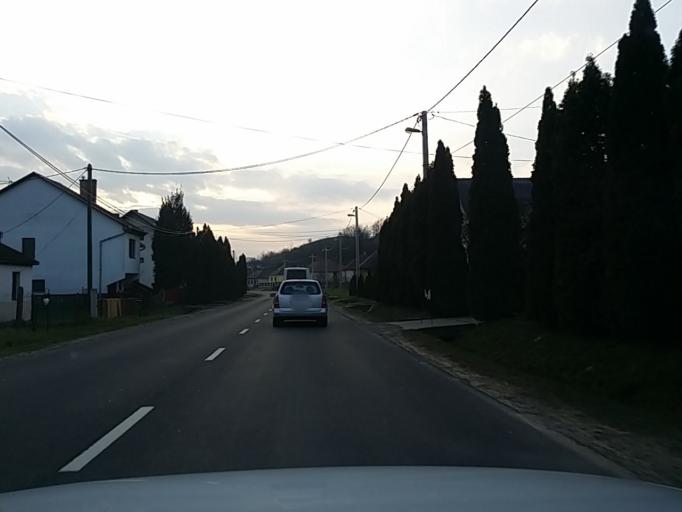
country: HU
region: Nograd
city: Matranovak
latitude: 48.0104
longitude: 19.9784
